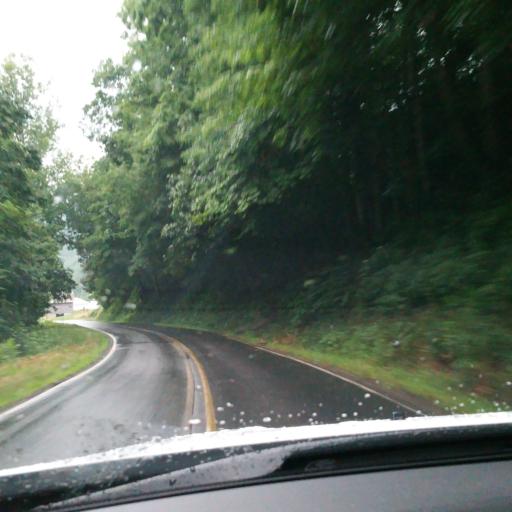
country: US
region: North Carolina
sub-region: Yancey County
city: Burnsville
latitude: 35.8876
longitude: -82.2819
